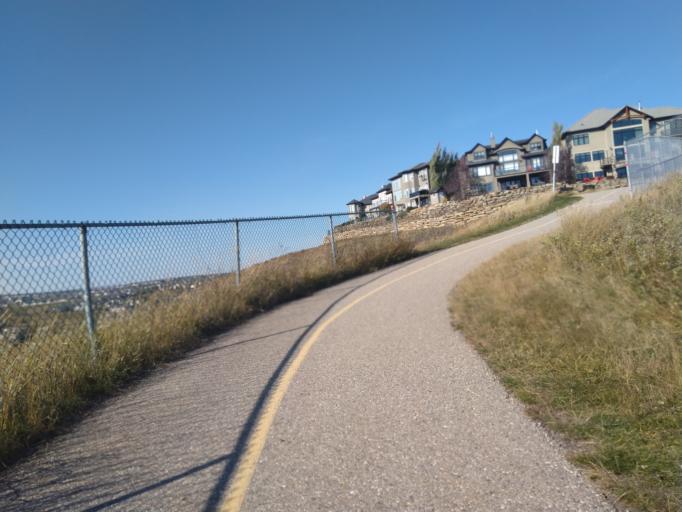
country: CA
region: Alberta
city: Calgary
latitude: 51.1506
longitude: -114.0930
